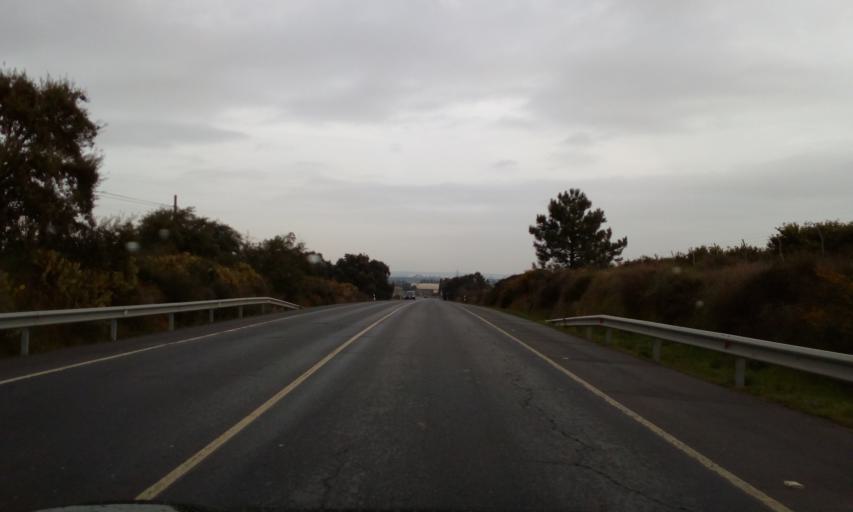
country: ES
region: Andalusia
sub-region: Provincia de Huelva
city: Lepe
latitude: 37.2741
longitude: -7.1885
